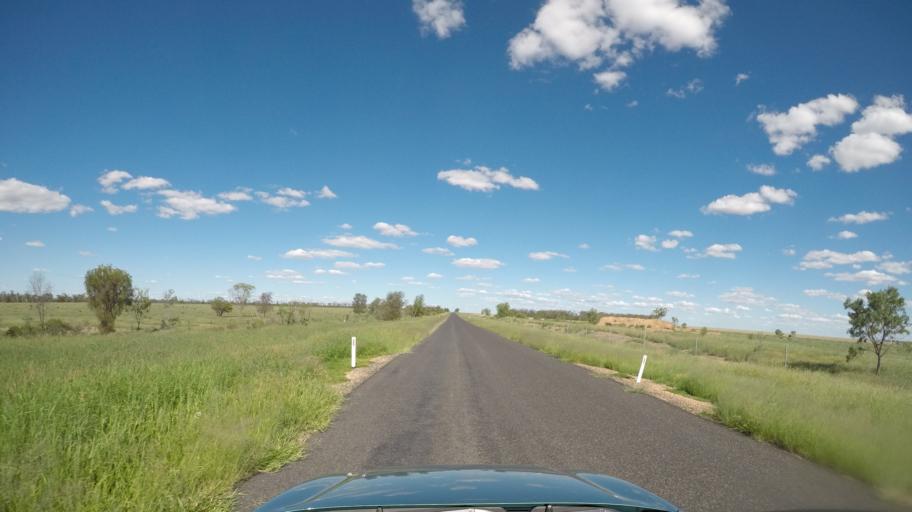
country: AU
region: Queensland
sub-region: Goondiwindi
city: Goondiwindi
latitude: -28.1602
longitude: 150.1310
